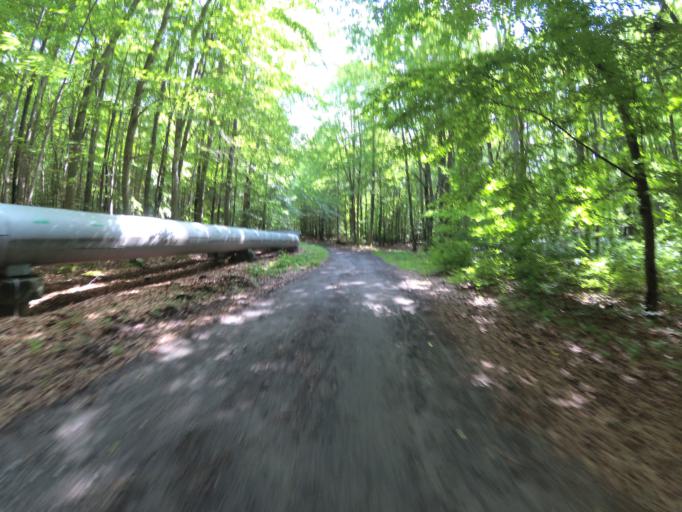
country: PL
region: Pomeranian Voivodeship
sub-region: Gdynia
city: Wielki Kack
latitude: 54.5070
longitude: 18.4902
